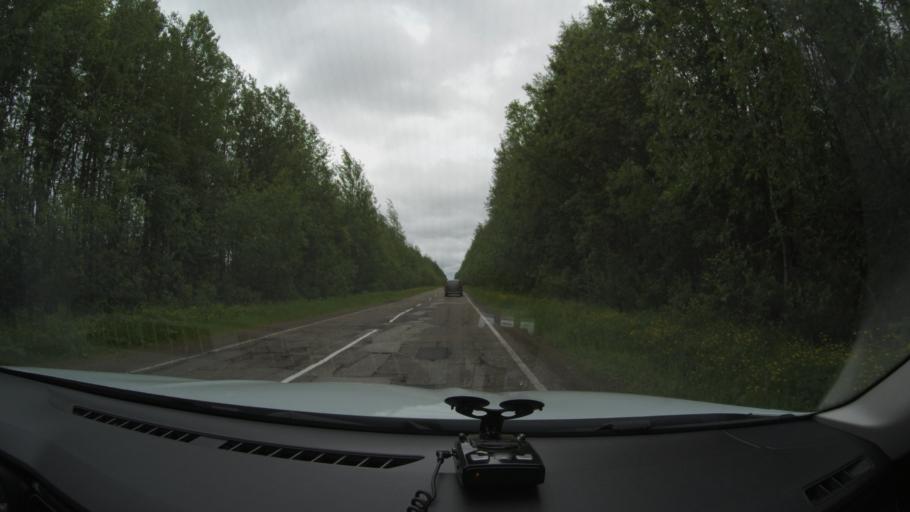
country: RU
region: Komi Republic
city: Sosnogorsk
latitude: 63.6025
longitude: 54.3470
